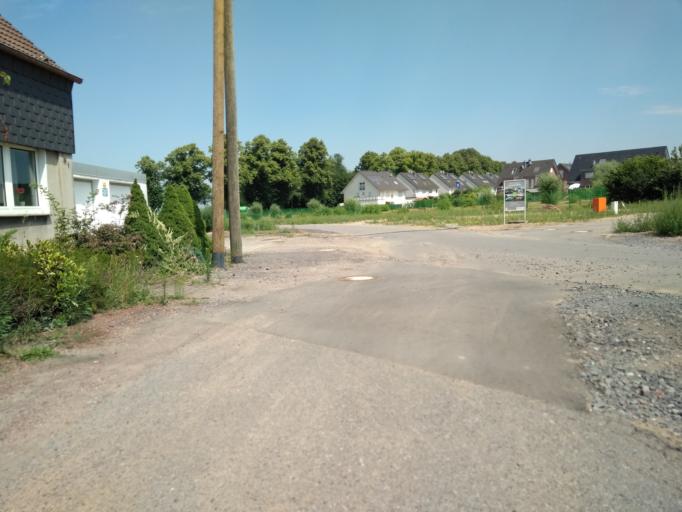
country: DE
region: North Rhine-Westphalia
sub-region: Regierungsbezirk Munster
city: Gladbeck
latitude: 51.6105
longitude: 6.9627
